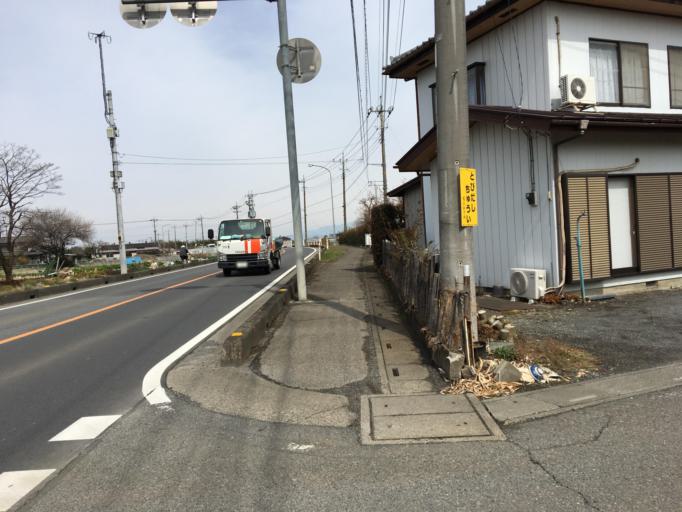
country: JP
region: Saitama
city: Yorii
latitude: 36.1391
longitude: 139.2124
